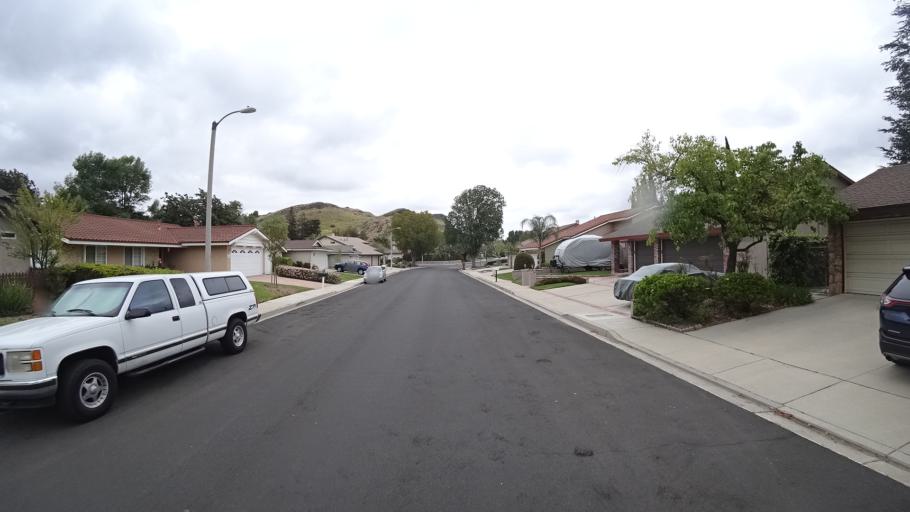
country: US
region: California
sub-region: Ventura County
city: Casa Conejo
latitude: 34.2234
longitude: -118.8971
